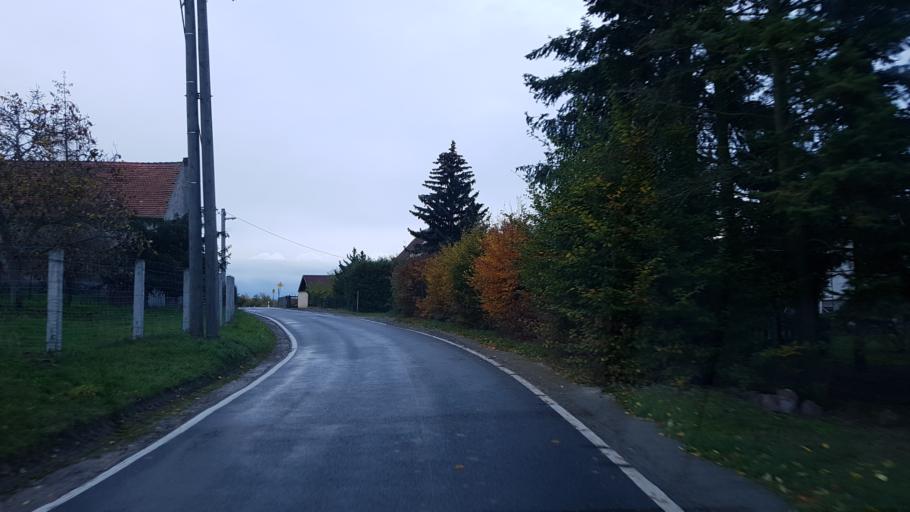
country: DE
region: Saxony
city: Belgern
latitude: 51.4395
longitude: 13.0885
